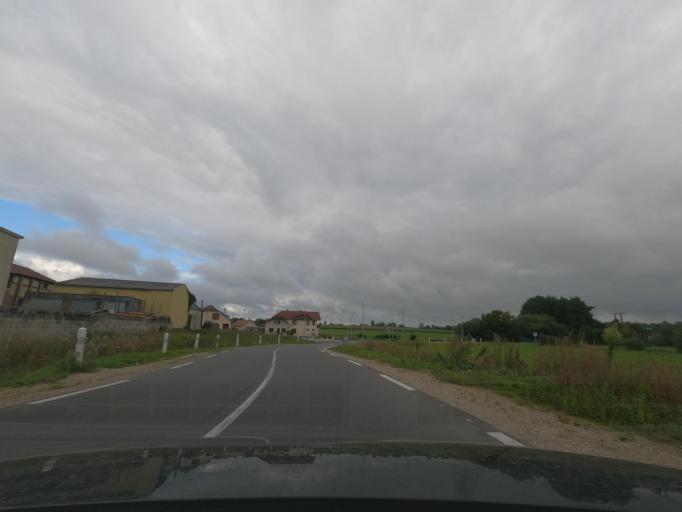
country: FR
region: Haute-Normandie
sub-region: Departement de la Seine-Maritime
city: Forges-les-Eaux
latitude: 49.6155
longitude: 1.5558
